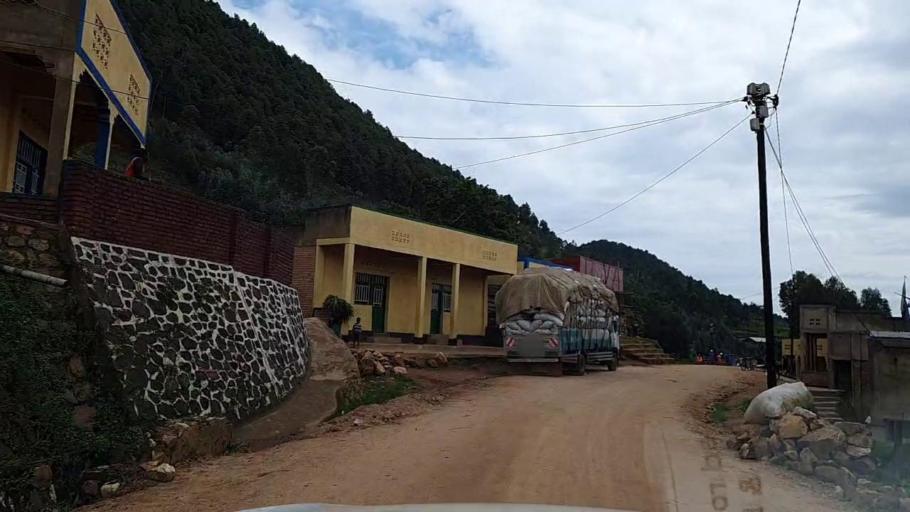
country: RW
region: Southern Province
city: Nzega
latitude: -2.3985
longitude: 29.4538
